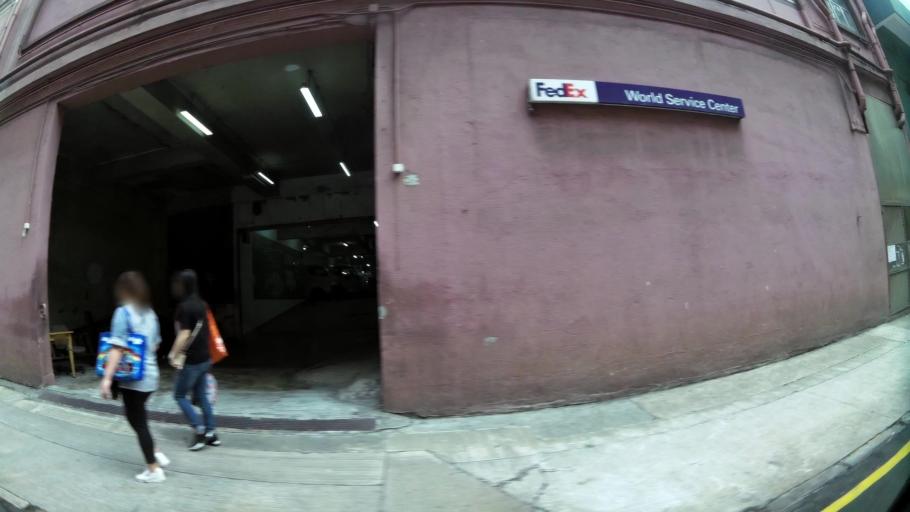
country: HK
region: Wanchai
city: Wan Chai
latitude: 22.2652
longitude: 114.2355
